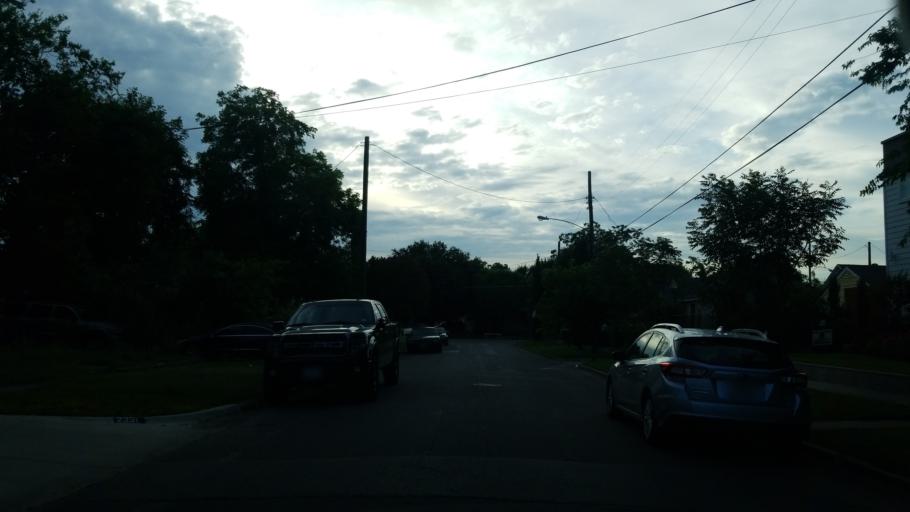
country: US
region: Texas
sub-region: Dallas County
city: Highland Park
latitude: 32.8093
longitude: -96.7834
